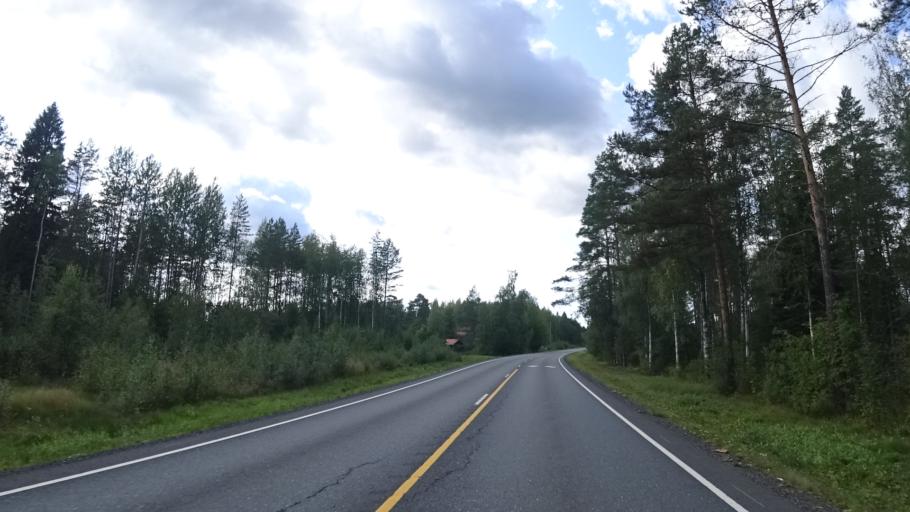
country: FI
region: North Karelia
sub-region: Keski-Karjala
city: Tohmajaervi
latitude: 62.1762
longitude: 30.5379
